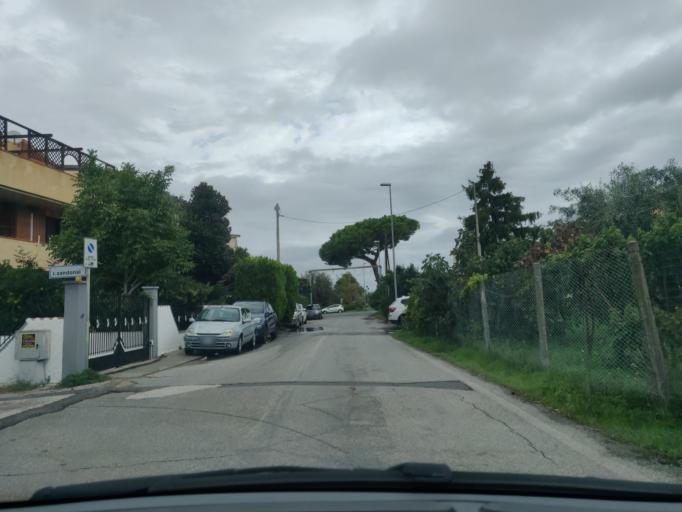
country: IT
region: Latium
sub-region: Citta metropolitana di Roma Capitale
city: Aurelia
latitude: 42.1372
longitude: 11.7884
